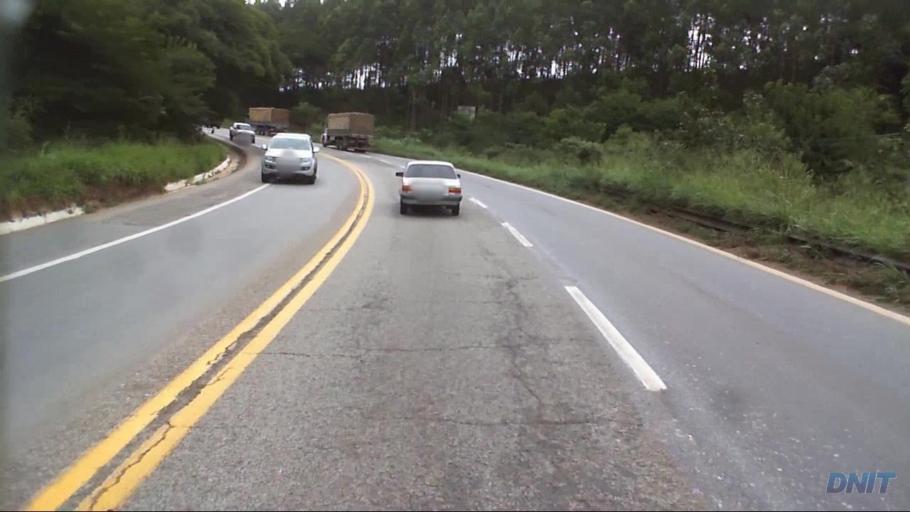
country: BR
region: Minas Gerais
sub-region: Caete
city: Caete
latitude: -19.7513
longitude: -43.5360
